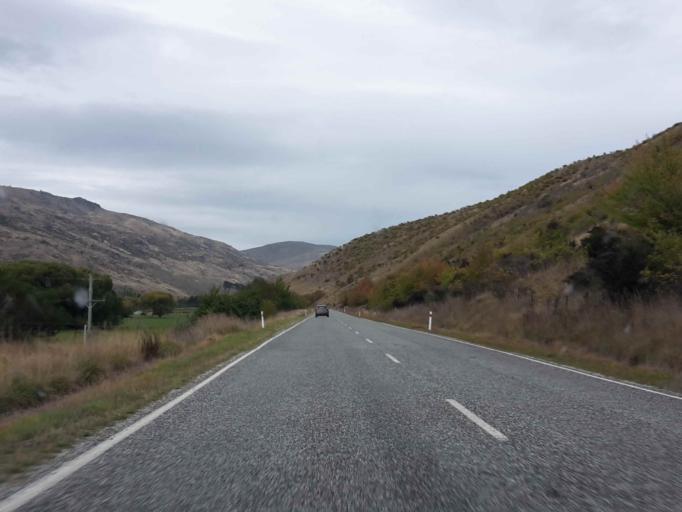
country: NZ
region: Otago
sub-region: Queenstown-Lakes District
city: Wanaka
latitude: -44.8133
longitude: 169.0652
